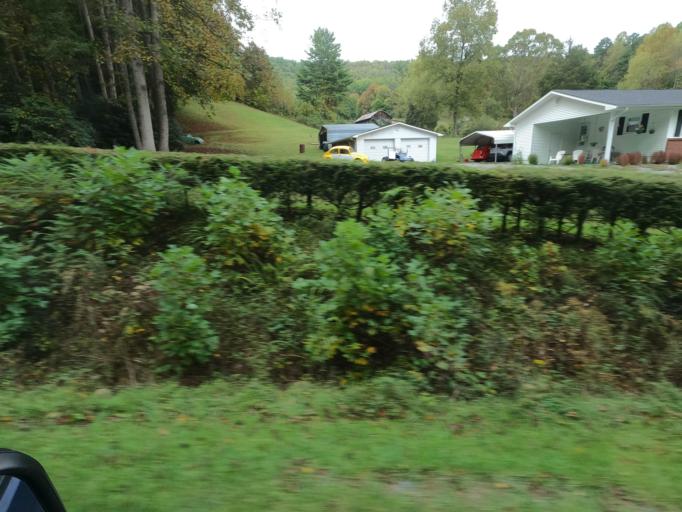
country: US
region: Tennessee
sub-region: Carter County
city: Elizabethton
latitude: 36.2616
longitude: -82.2088
